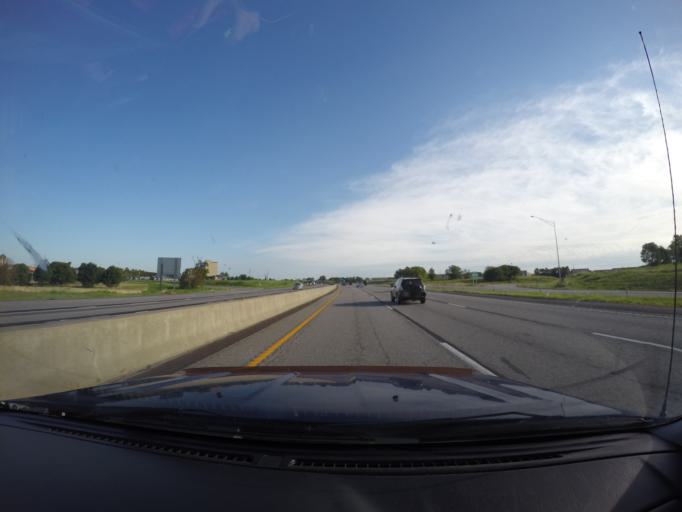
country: US
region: Missouri
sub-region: Platte County
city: Weatherby Lake
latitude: 39.2552
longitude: -94.6584
